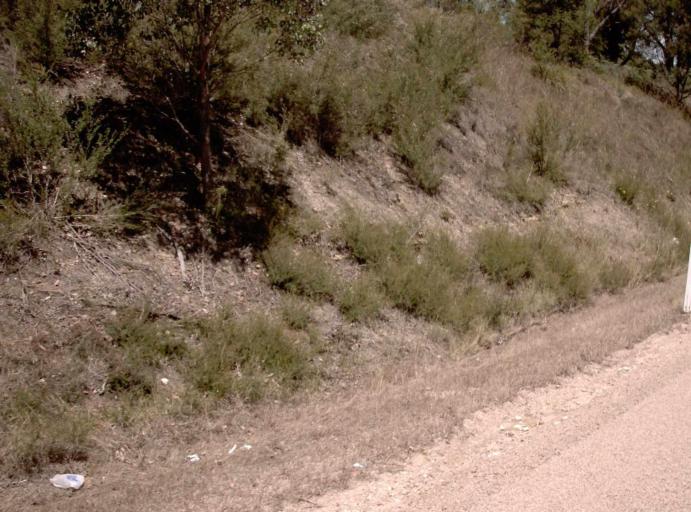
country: AU
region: Victoria
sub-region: East Gippsland
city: Bairnsdale
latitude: -37.7489
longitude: 147.7525
